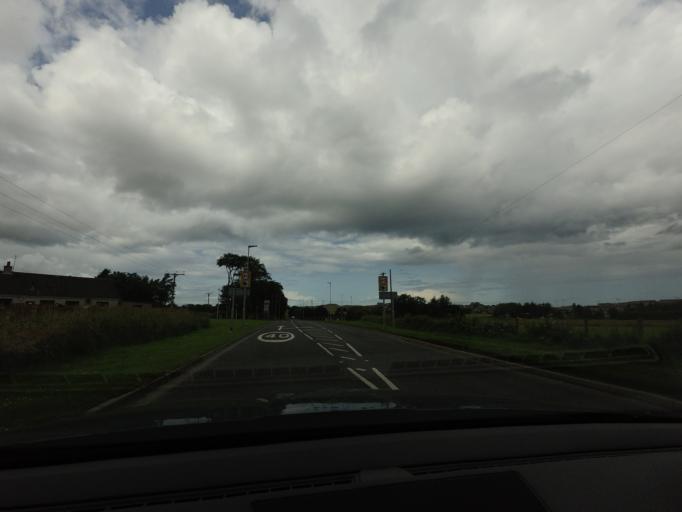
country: GB
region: Scotland
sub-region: Aberdeenshire
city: Macduff
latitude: 57.6582
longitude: -2.4887
